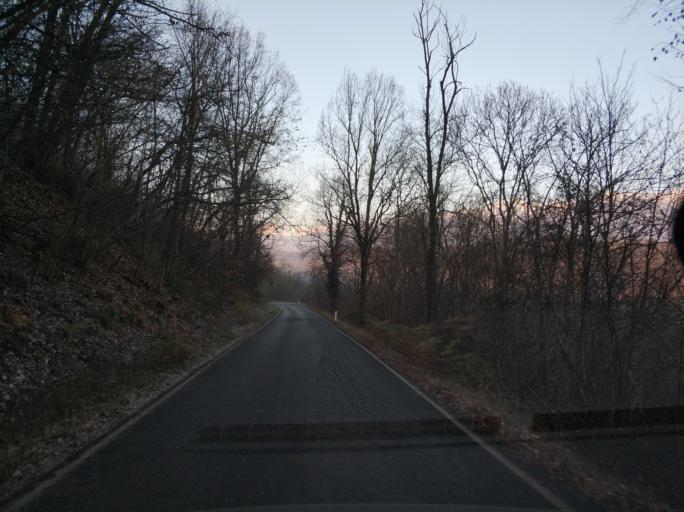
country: IT
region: Piedmont
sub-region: Provincia di Torino
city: Barbania
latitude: 45.2847
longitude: 7.6346
